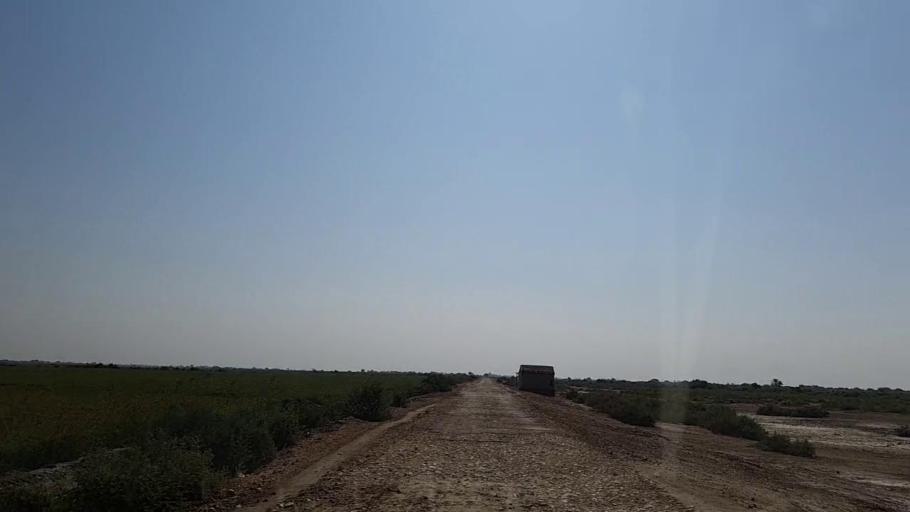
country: PK
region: Sindh
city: Chuhar Jamali
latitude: 24.4722
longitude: 68.0917
